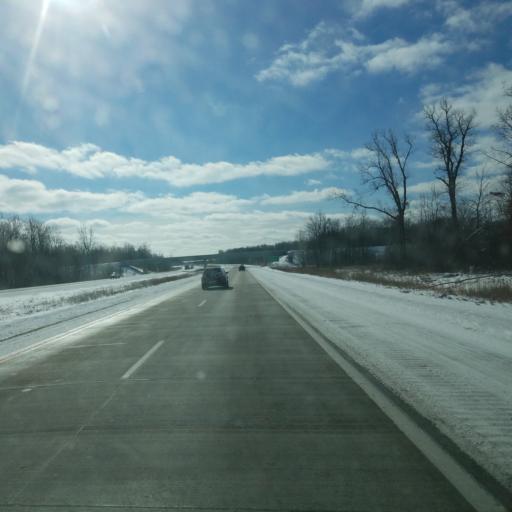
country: US
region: Michigan
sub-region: Clinton County
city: DeWitt
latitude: 42.8735
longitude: -84.5175
